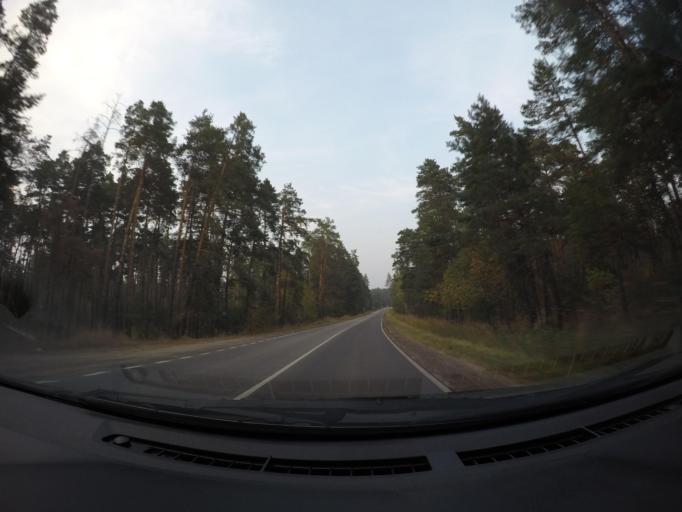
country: RU
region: Moskovskaya
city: Imeni Tsyurupy
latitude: 55.4949
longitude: 38.6839
